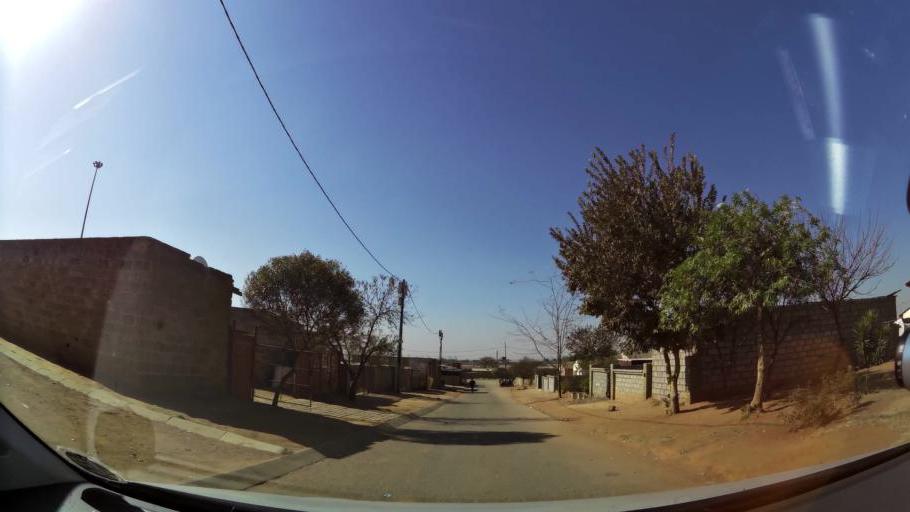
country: ZA
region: Gauteng
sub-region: Ekurhuleni Metropolitan Municipality
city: Tembisa
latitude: -26.0239
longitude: 28.2422
